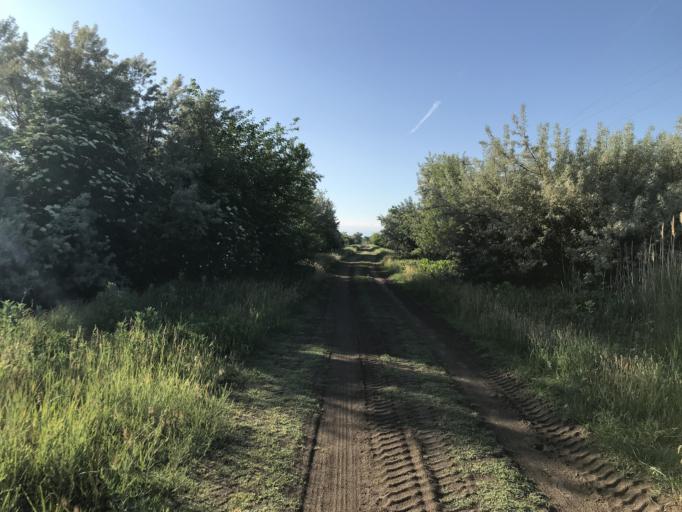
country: HU
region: Bacs-Kiskun
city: Tiszakecske
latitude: 46.9731
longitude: 20.0616
